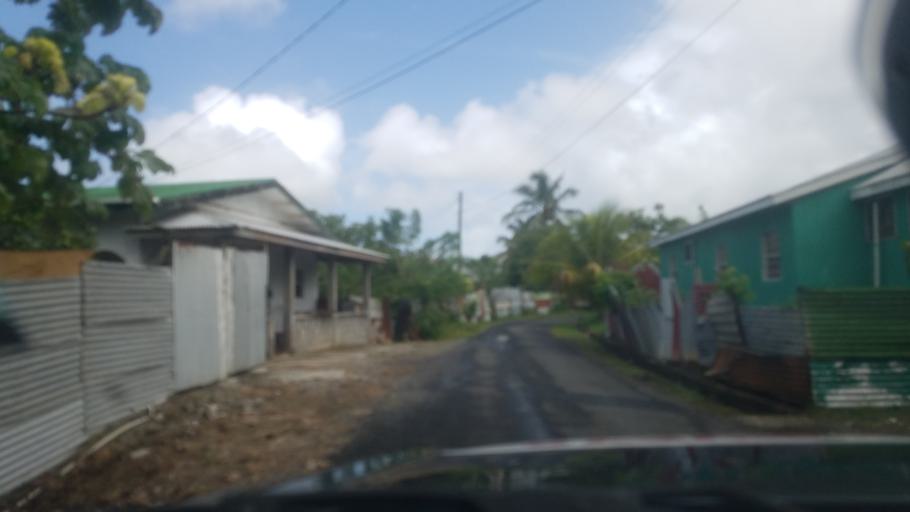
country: LC
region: Laborie Quarter
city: Laborie
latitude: 13.7501
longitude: -60.9670
